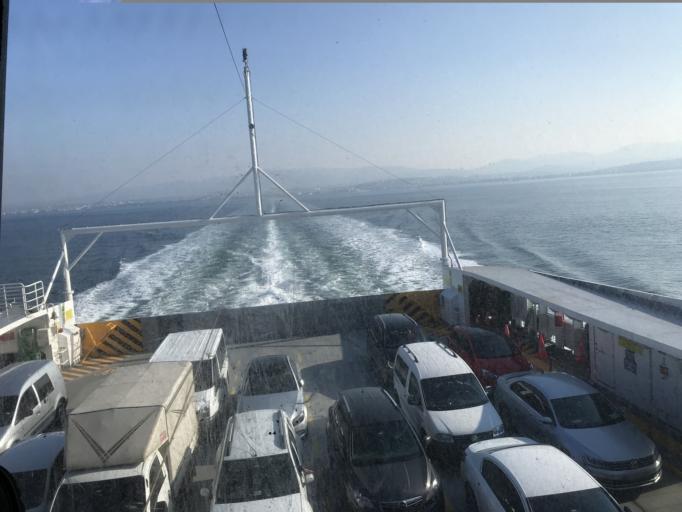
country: TR
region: Yalova
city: Yalova
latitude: 40.6946
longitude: 29.2520
